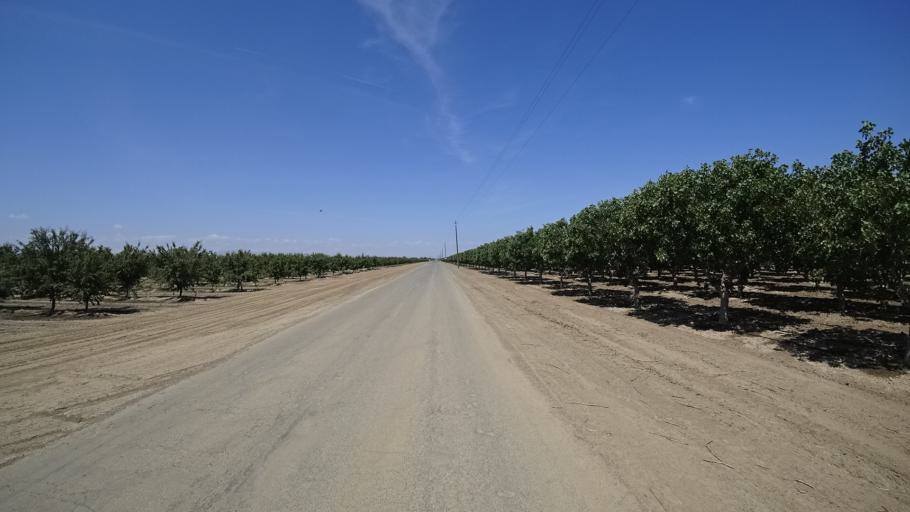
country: US
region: California
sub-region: Kings County
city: Kettleman City
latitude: 36.0943
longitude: -119.9857
